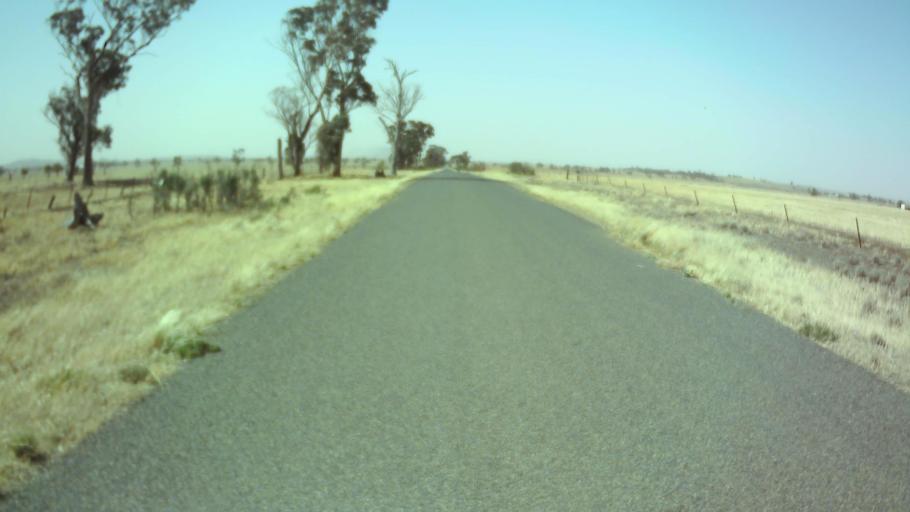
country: AU
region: New South Wales
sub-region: Weddin
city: Grenfell
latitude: -33.8822
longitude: 147.9242
